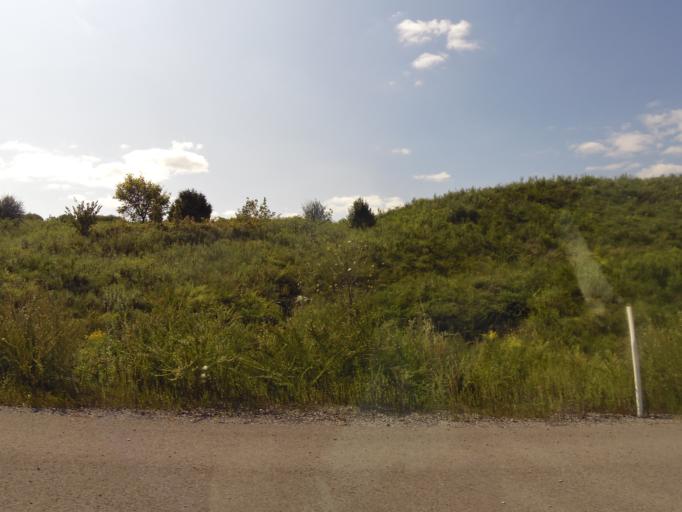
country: US
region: Kentucky
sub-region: Bell County
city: Pineville
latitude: 36.7336
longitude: -83.5901
